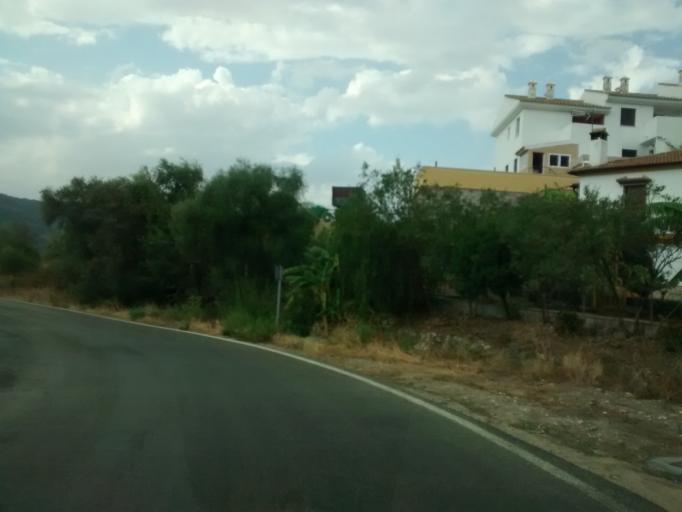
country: ES
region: Andalusia
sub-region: Provincia de Cadiz
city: El Bosque
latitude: 36.7538
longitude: -5.5066
